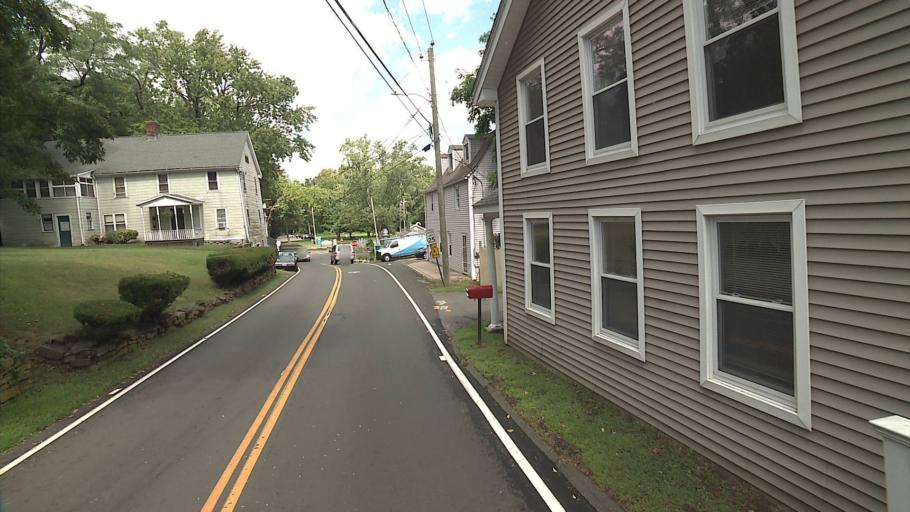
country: US
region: Connecticut
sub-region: Hartford County
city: Glastonbury Center
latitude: 41.6657
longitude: -72.6302
